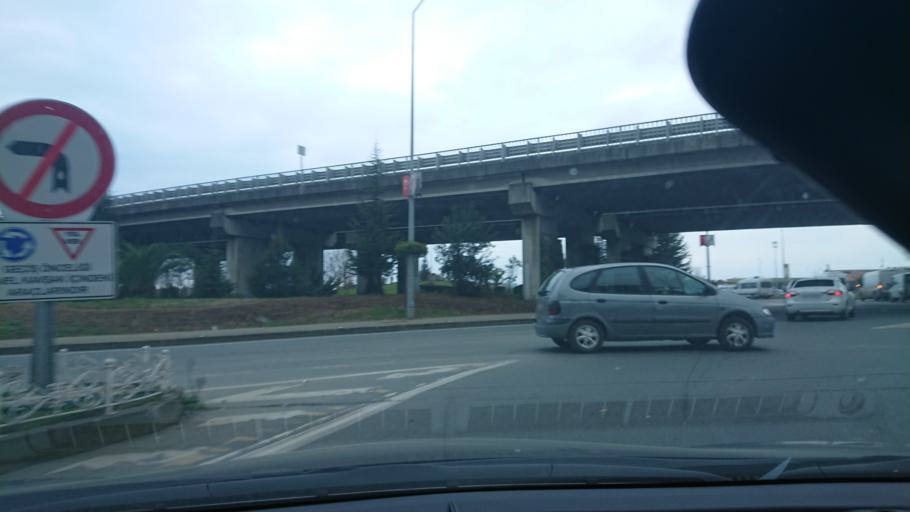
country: TR
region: Rize
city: Rize
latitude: 41.0260
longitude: 40.5208
